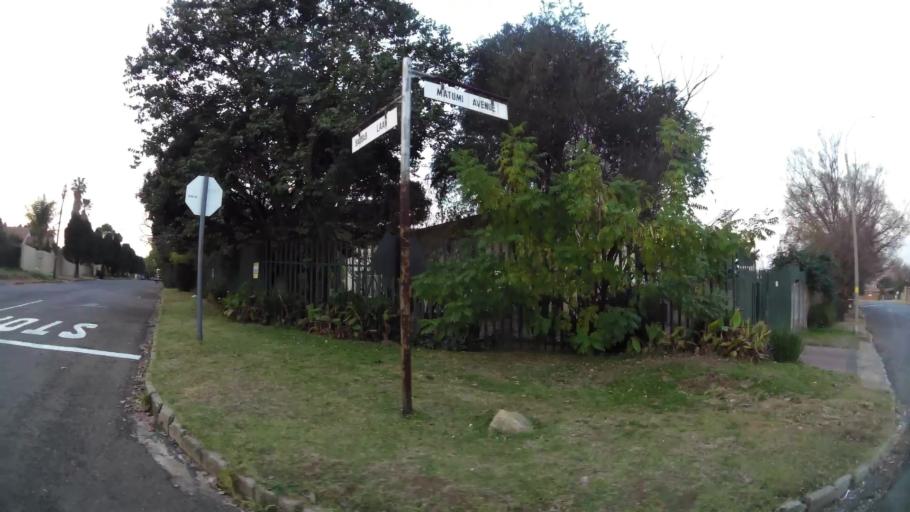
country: ZA
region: Gauteng
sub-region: Ekurhuleni Metropolitan Municipality
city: Tembisa
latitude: -26.0616
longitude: 28.2371
